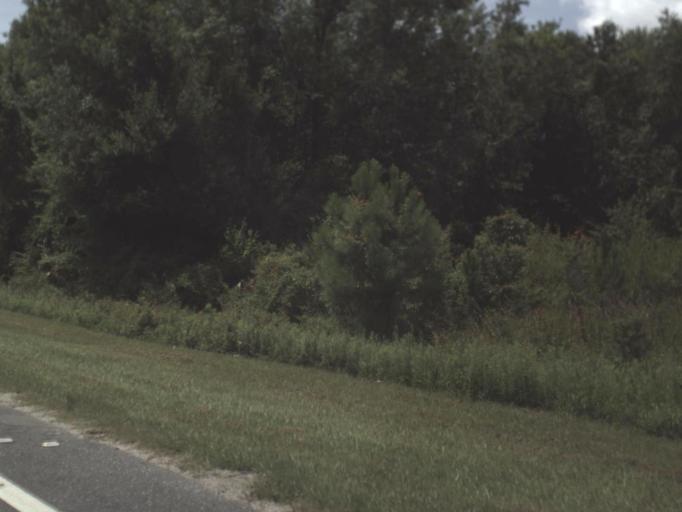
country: US
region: Florida
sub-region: Taylor County
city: Perry
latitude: 30.0669
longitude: -83.5588
